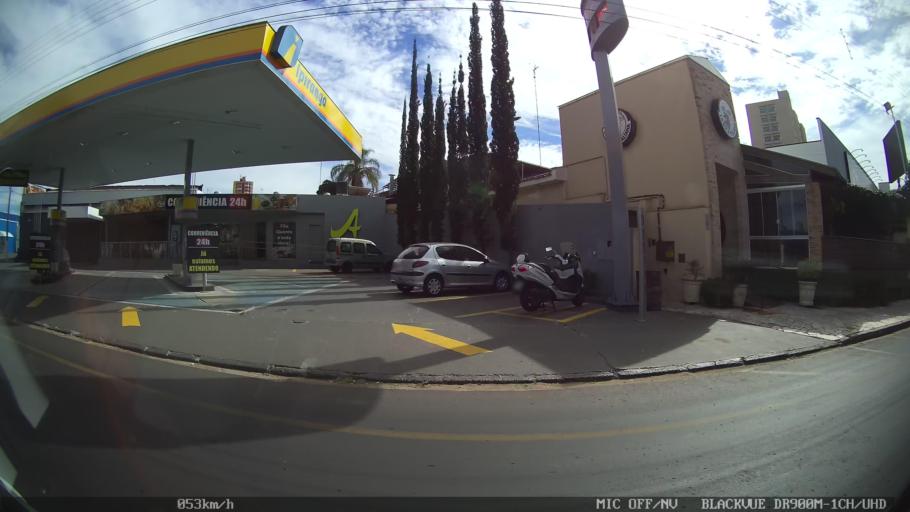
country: BR
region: Sao Paulo
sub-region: Catanduva
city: Catanduva
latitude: -21.1454
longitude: -48.9738
